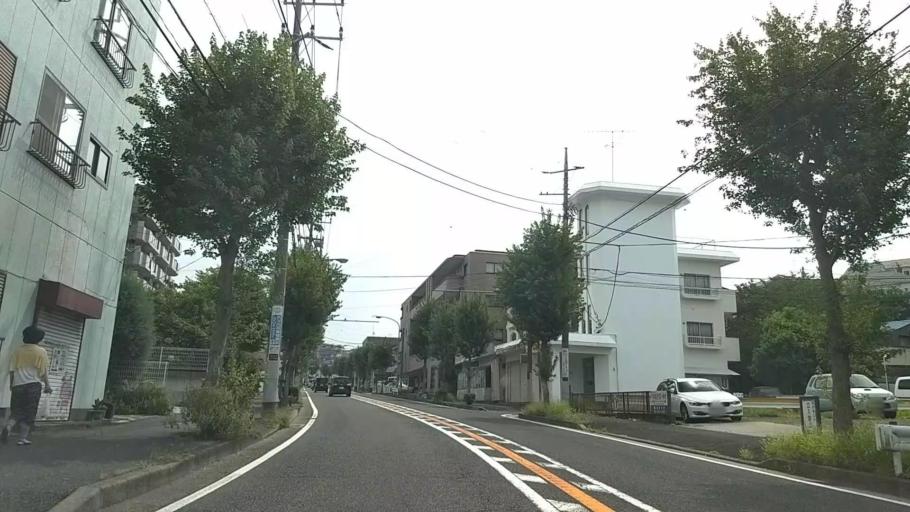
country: JP
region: Kanagawa
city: Yokohama
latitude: 35.4250
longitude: 139.5710
